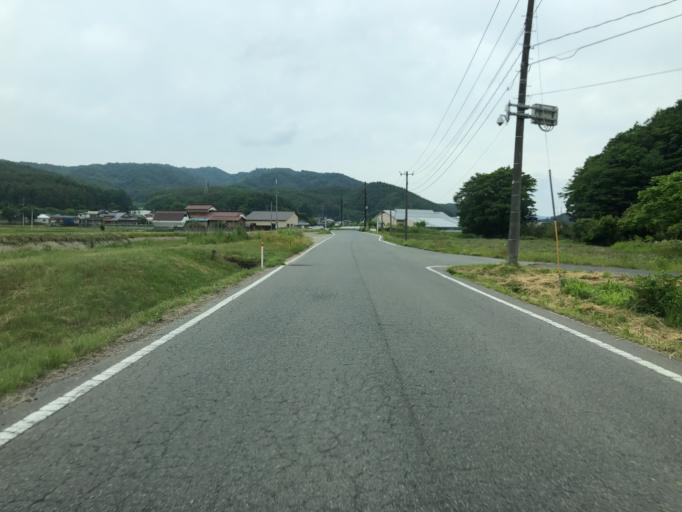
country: JP
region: Fukushima
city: Namie
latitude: 37.3463
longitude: 140.7996
